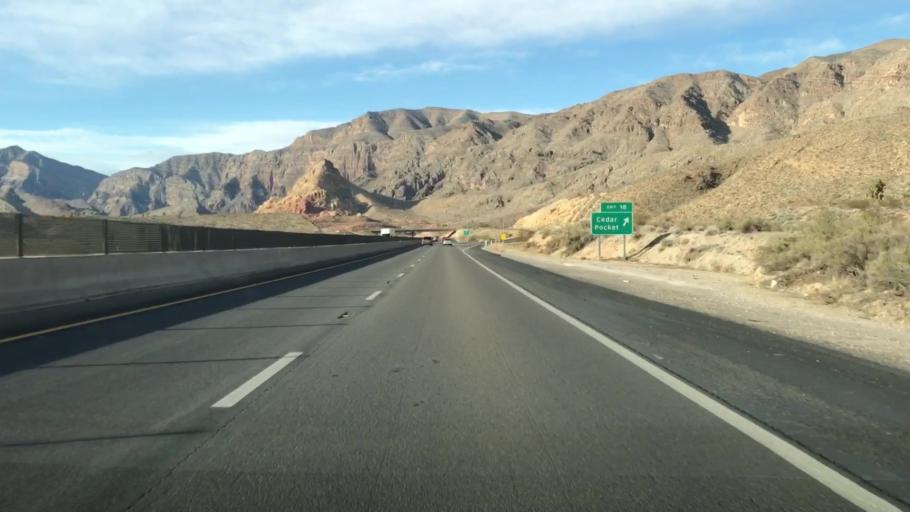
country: US
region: Arizona
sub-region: Mohave County
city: Beaver Dam
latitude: 36.9567
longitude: -113.7905
